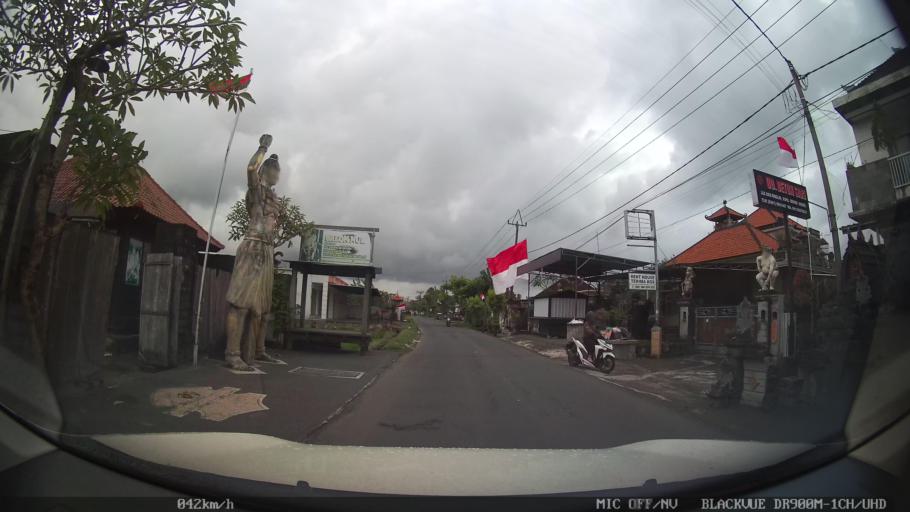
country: ID
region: Bali
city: Banjar Pekenjelodan
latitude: -8.5603
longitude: 115.1881
